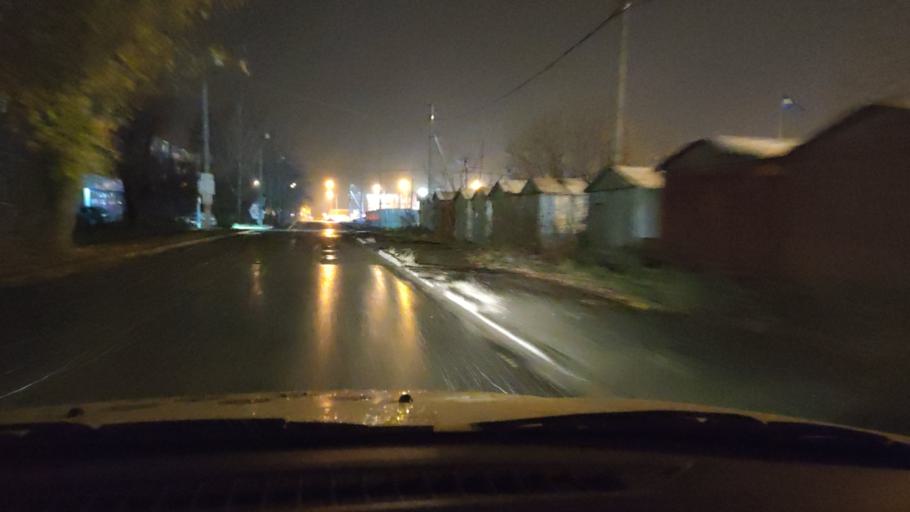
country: RU
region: Perm
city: Kondratovo
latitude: 57.9516
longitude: 56.1167
